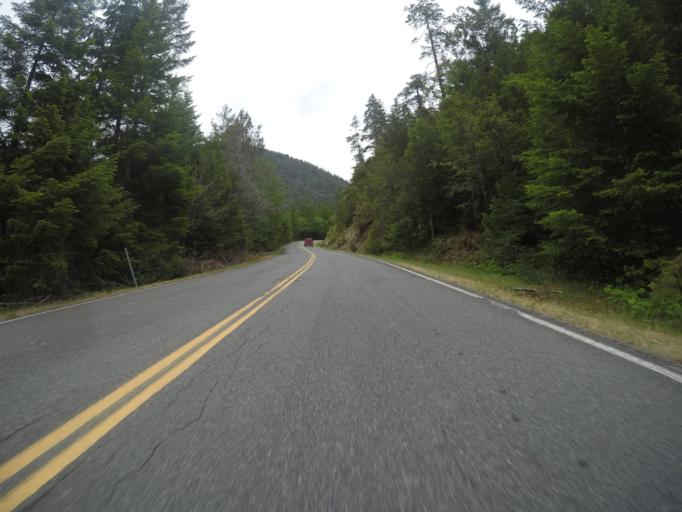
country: US
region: California
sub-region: Del Norte County
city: Bertsch-Oceanview
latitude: 41.7258
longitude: -123.9647
